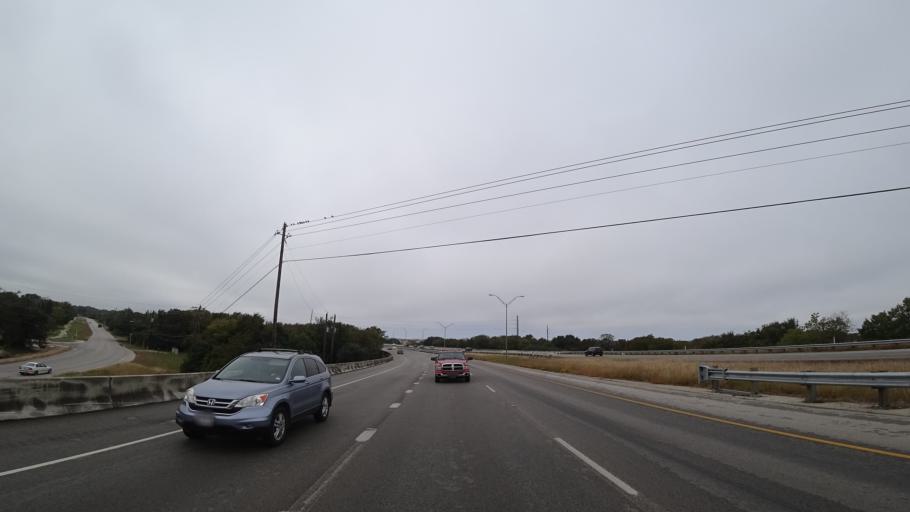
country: US
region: Texas
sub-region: Travis County
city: Shady Hollow
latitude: 30.2166
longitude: -97.8484
